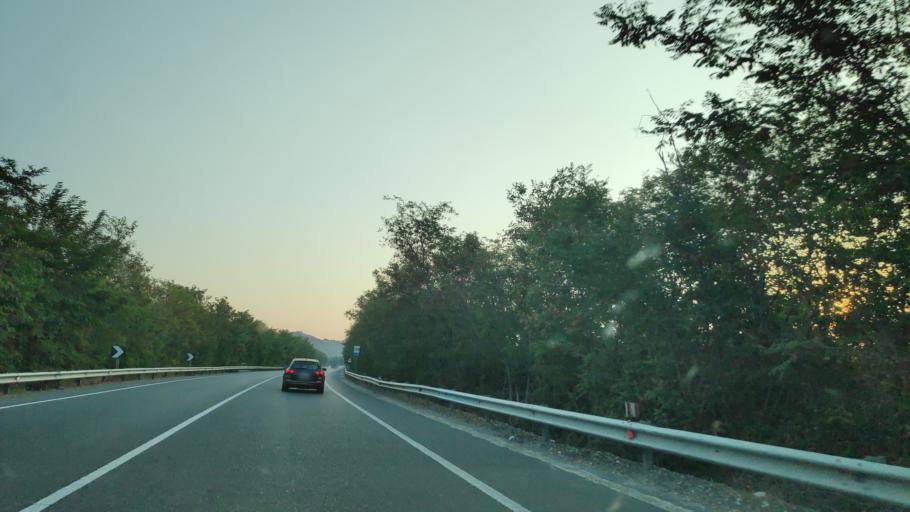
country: IT
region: Calabria
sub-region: Provincia di Catanzaro
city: Montepaone Lido
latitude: 38.7333
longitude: 16.5419
